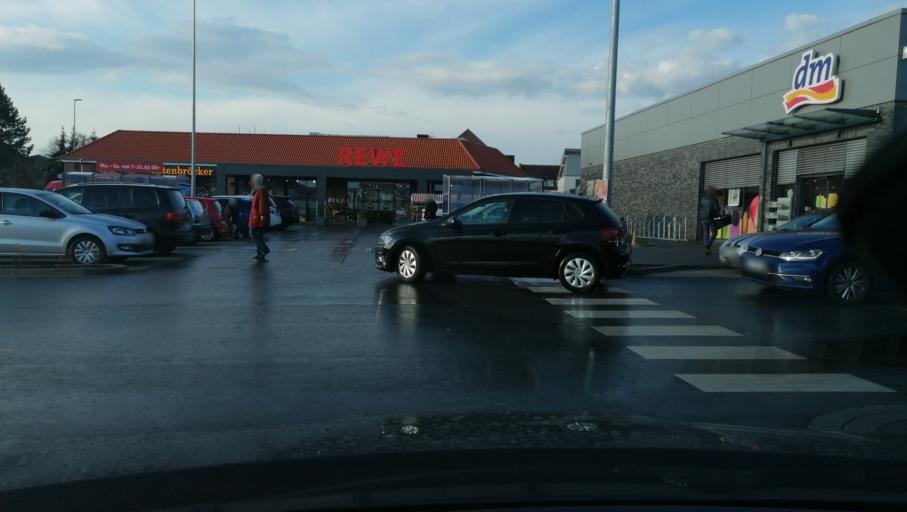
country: DE
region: North Rhine-Westphalia
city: Herten
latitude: 51.6025
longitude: 7.1549
